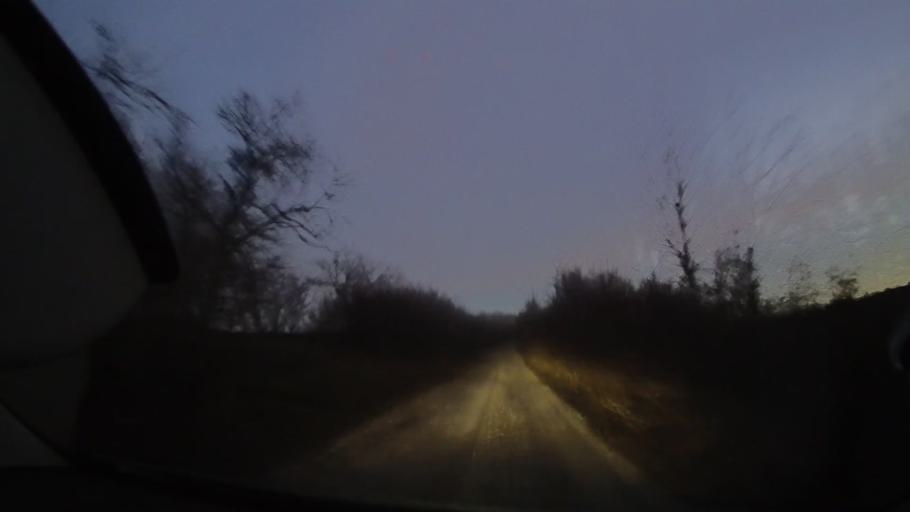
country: RO
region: Bihor
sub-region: Comuna Tetchea
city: Hotar
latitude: 47.0006
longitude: 22.3102
